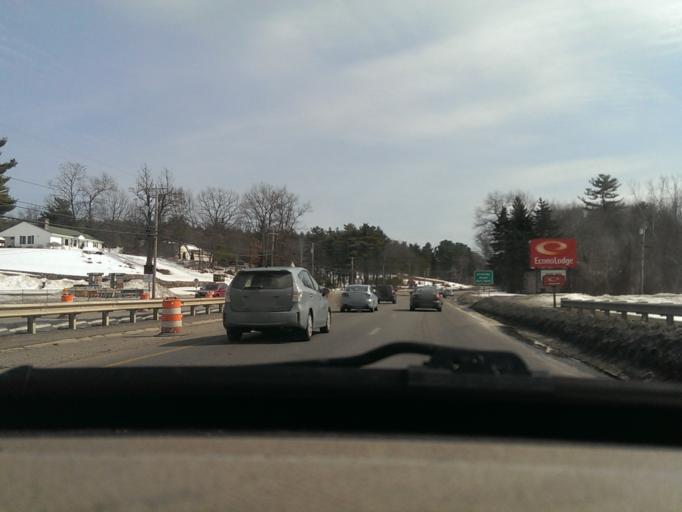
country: US
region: Massachusetts
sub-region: Worcester County
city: Sutton
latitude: 42.1577
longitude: -71.7318
